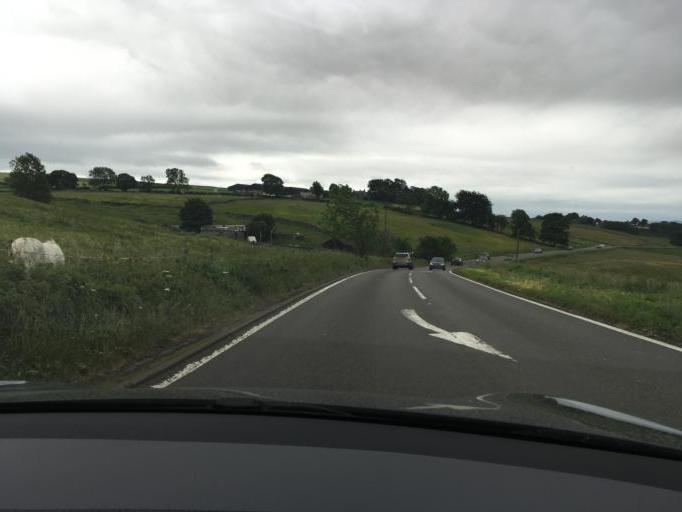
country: GB
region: England
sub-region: Derbyshire
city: Chapel en le Frith
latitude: 53.3222
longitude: -1.8652
